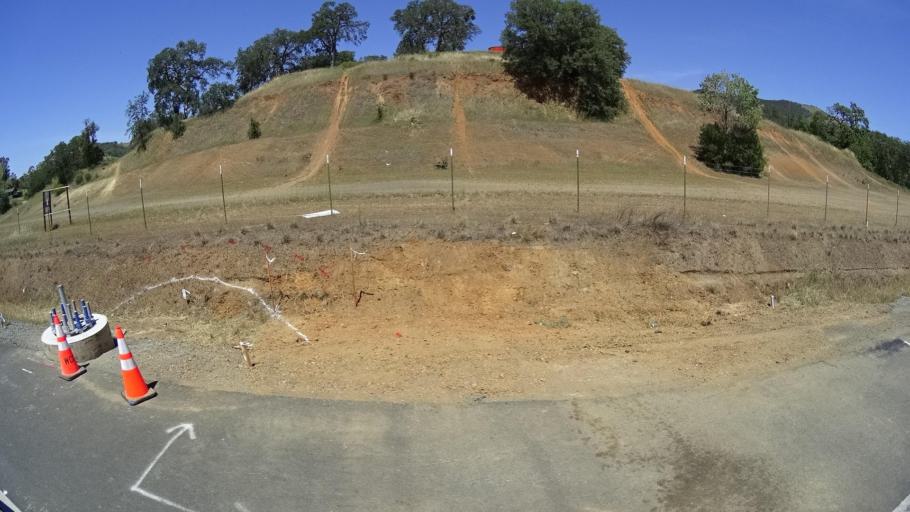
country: US
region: California
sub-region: Lake County
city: Nice
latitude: 39.1290
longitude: -122.8679
